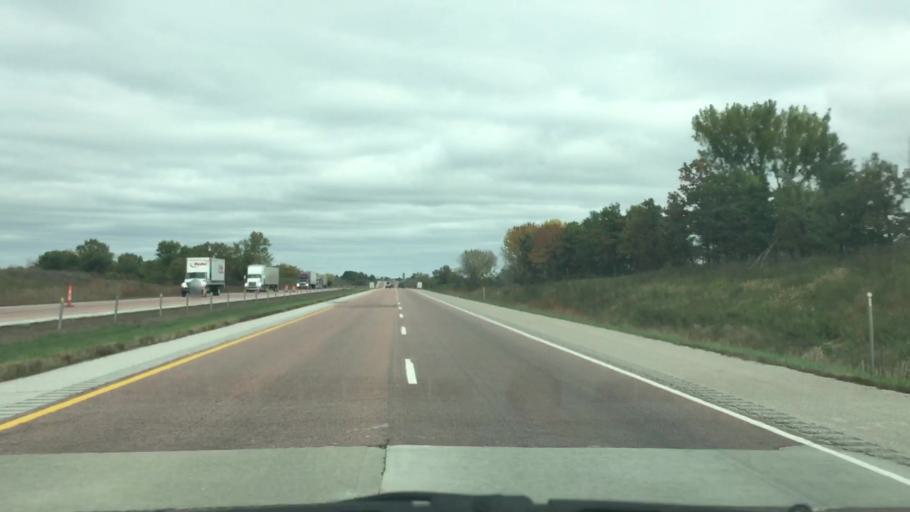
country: US
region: Iowa
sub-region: Clarke County
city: Osceola
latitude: 41.2602
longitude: -93.7819
